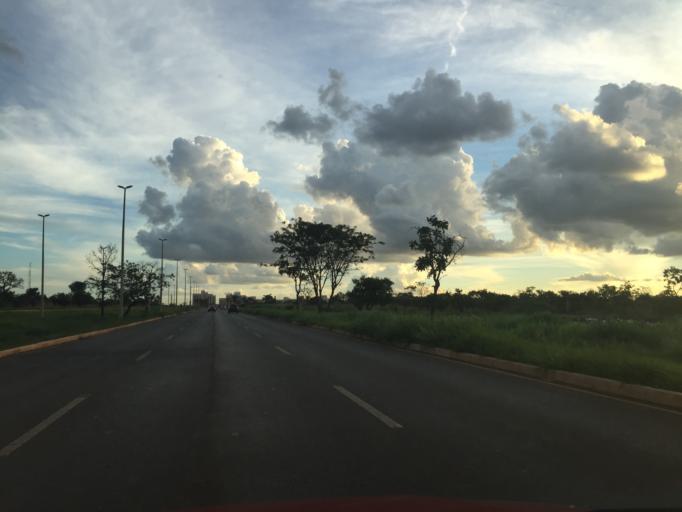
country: BR
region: Federal District
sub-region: Brasilia
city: Brasilia
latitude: -15.8051
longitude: -47.9921
